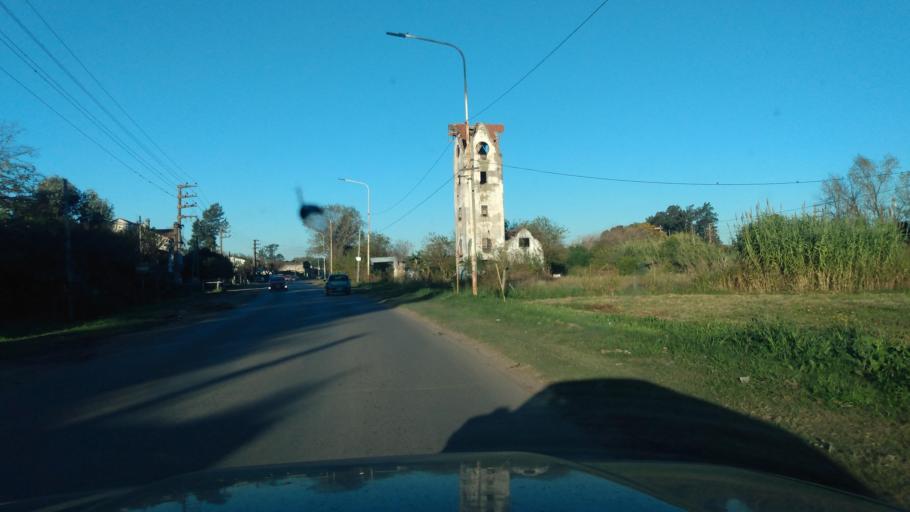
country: AR
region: Buenos Aires
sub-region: Partido de General Rodriguez
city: General Rodriguez
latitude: -34.6289
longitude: -58.8655
